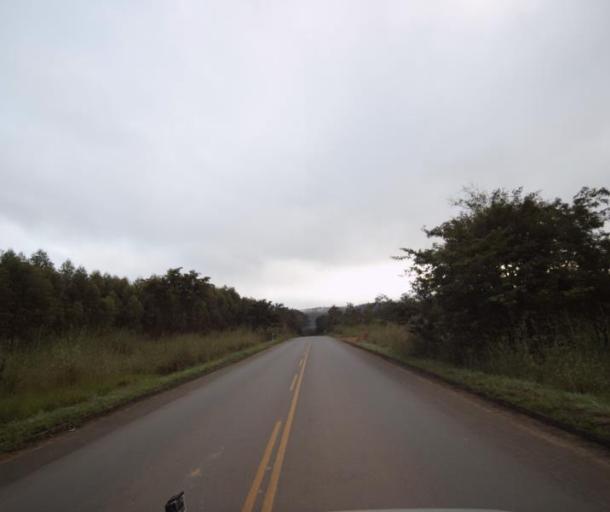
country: BR
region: Goias
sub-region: Pirenopolis
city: Pirenopolis
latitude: -15.8583
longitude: -48.7683
